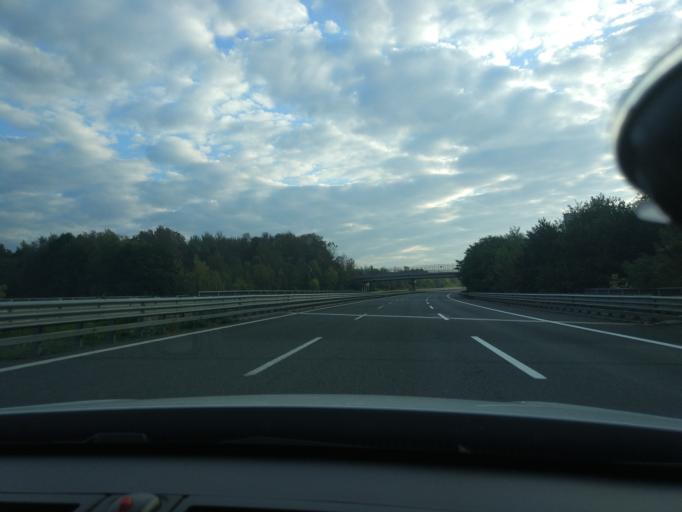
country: TR
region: Sakarya
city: Hendek
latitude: 40.7784
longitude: 30.7905
